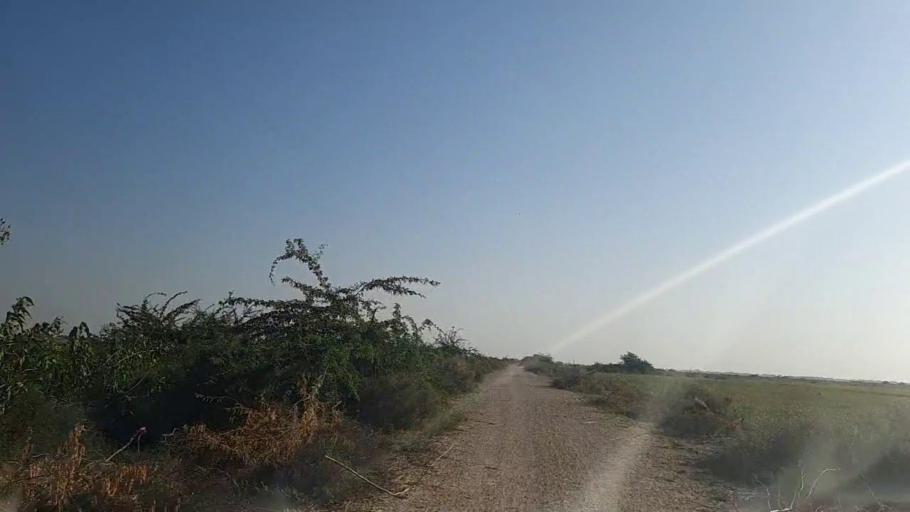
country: PK
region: Sindh
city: Jati
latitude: 24.3973
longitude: 68.2301
